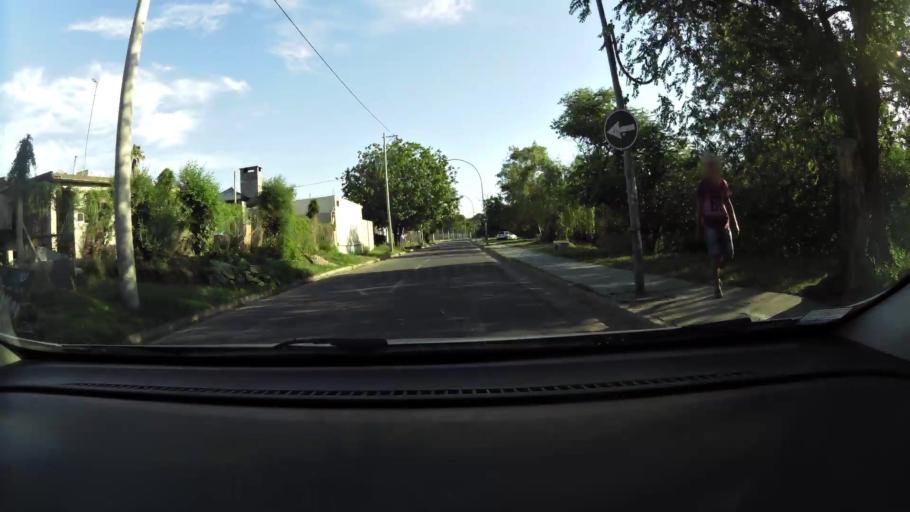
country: AR
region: Cordoba
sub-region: Departamento de Capital
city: Cordoba
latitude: -31.3796
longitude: -64.2489
